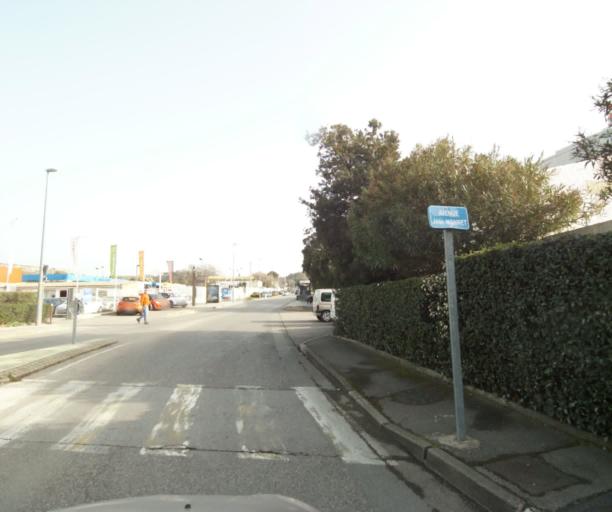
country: FR
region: Provence-Alpes-Cote d'Azur
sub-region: Departement des Bouches-du-Rhone
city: Les Pennes-Mirabeau
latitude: 43.4179
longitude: 5.2927
